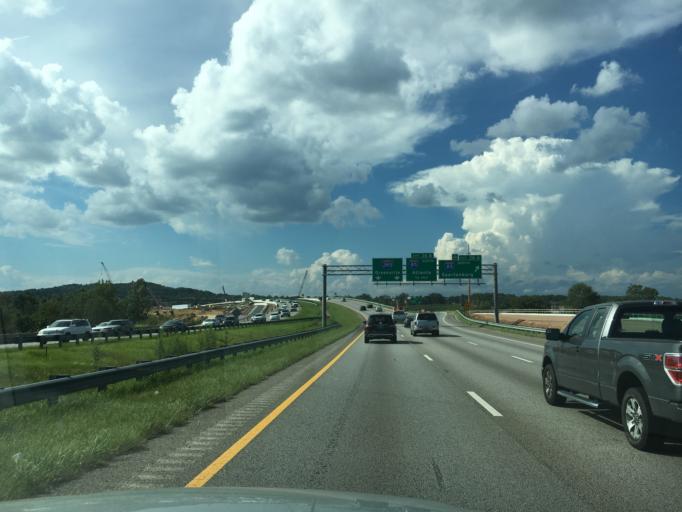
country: US
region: South Carolina
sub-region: Greenville County
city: Mauldin
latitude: 34.8290
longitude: -82.2937
